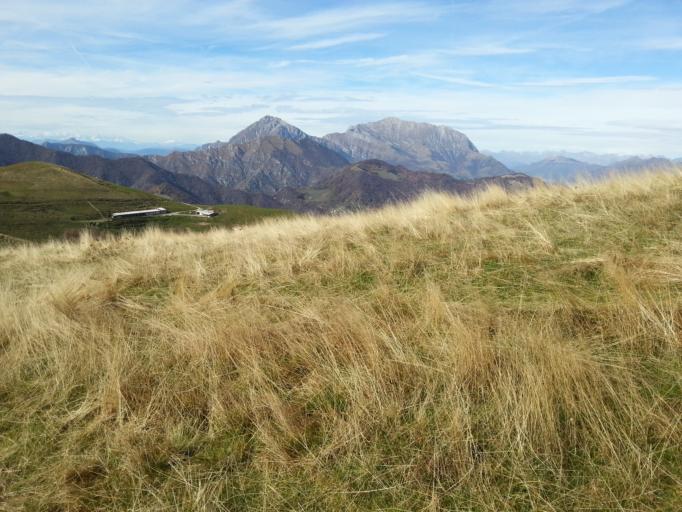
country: IT
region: Lombardy
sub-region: Provincia di Bergamo
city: Fuipiano Valle Imagna
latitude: 45.8697
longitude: 9.5199
